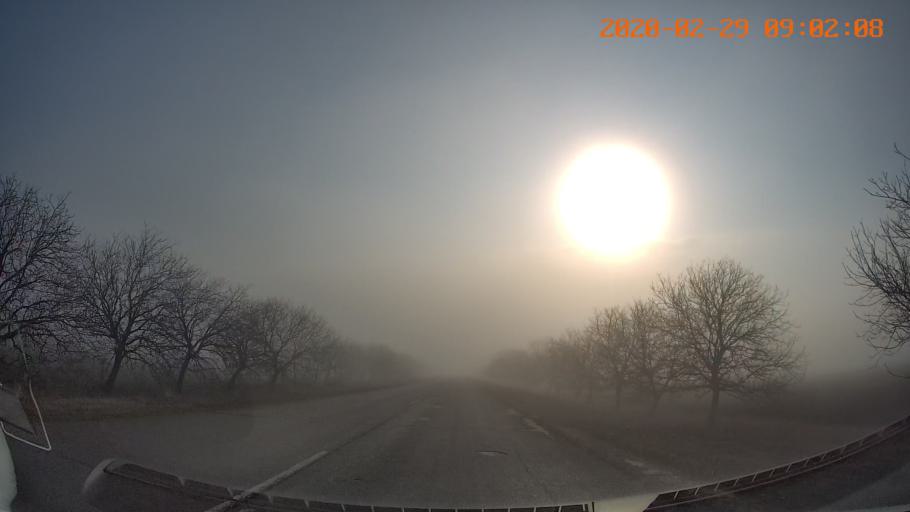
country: UA
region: Odessa
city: Velykoploske
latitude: 46.9221
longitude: 29.7052
